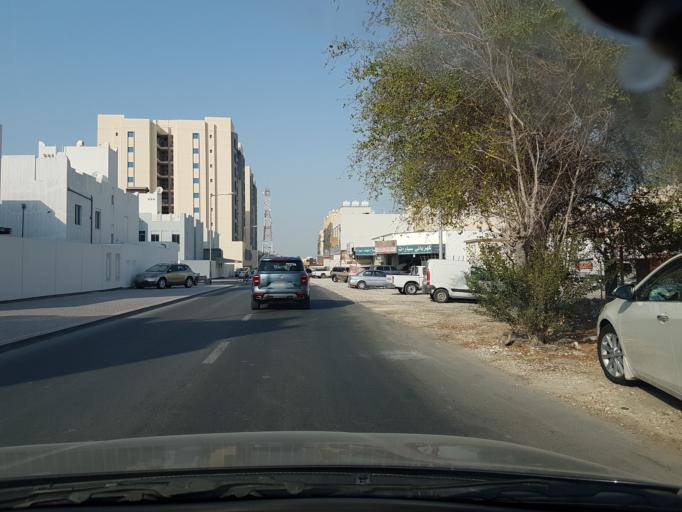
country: BH
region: Northern
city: Ar Rifa'
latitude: 26.1321
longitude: 50.5825
